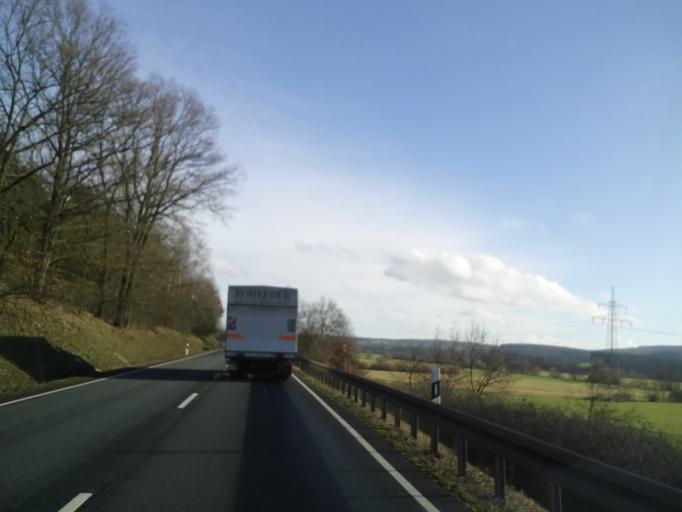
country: DE
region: Bavaria
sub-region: Upper Franconia
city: Altenkunstadt
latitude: 50.1292
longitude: 11.2641
